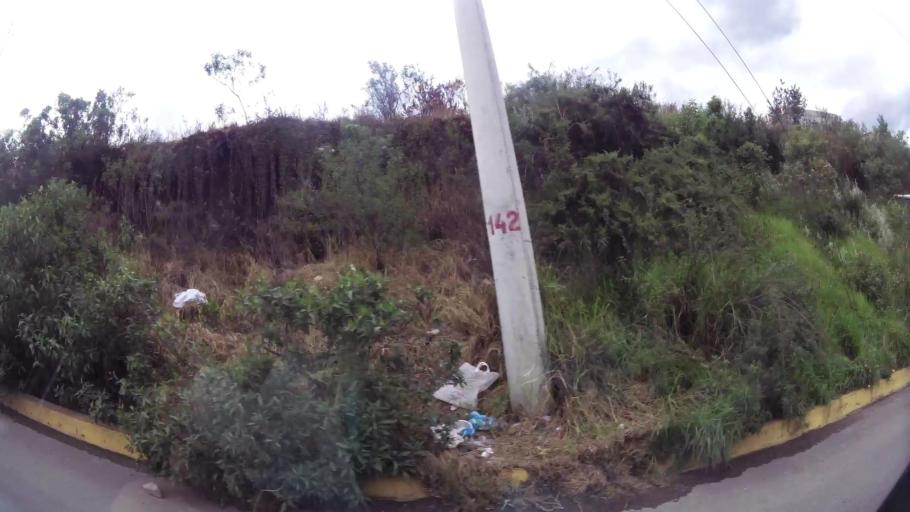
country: EC
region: Pichincha
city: Sangolqui
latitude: -0.3294
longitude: -78.5255
